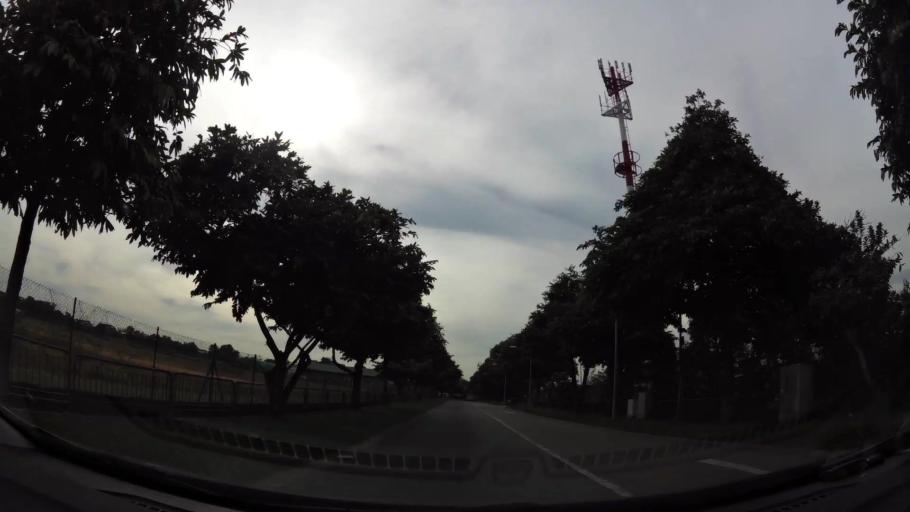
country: MY
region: Johor
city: Johor Bahru
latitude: 1.4353
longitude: 103.7131
